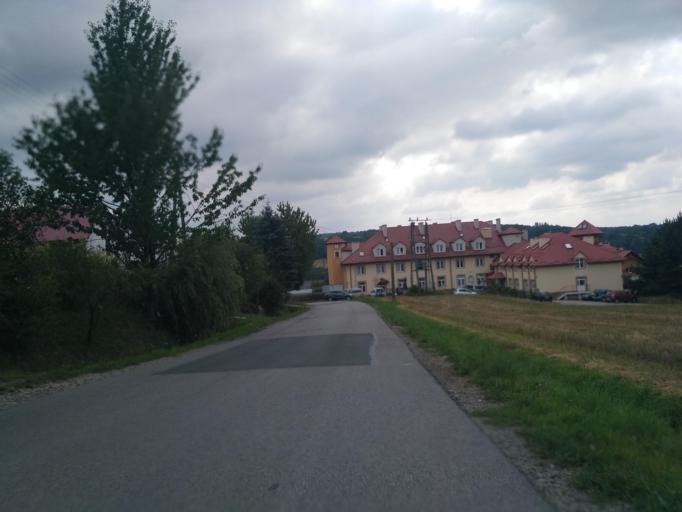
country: PL
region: Subcarpathian Voivodeship
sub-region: Powiat rzeszowski
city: Chmielnik
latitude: 49.9847
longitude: 22.1193
